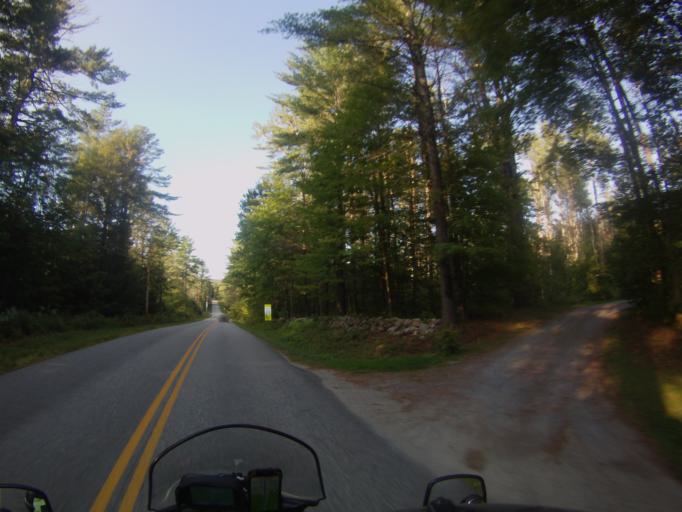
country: US
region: Vermont
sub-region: Addison County
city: Middlebury (village)
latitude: 43.9815
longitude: -73.0384
